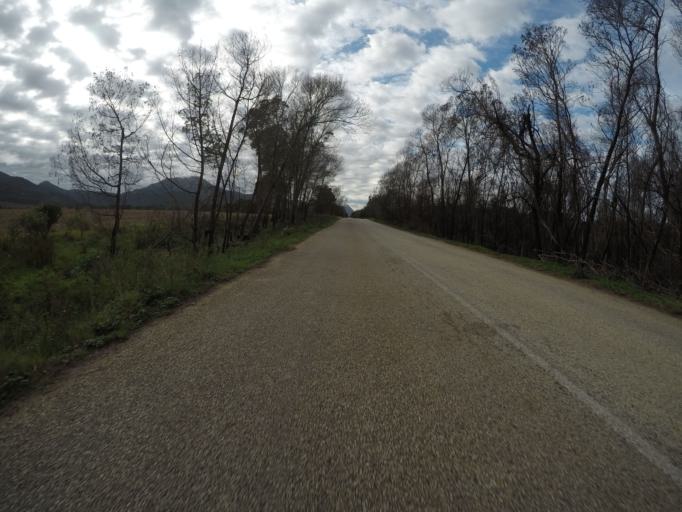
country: ZA
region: Eastern Cape
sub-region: Cacadu District Municipality
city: Kareedouw
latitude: -34.0154
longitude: 24.3265
